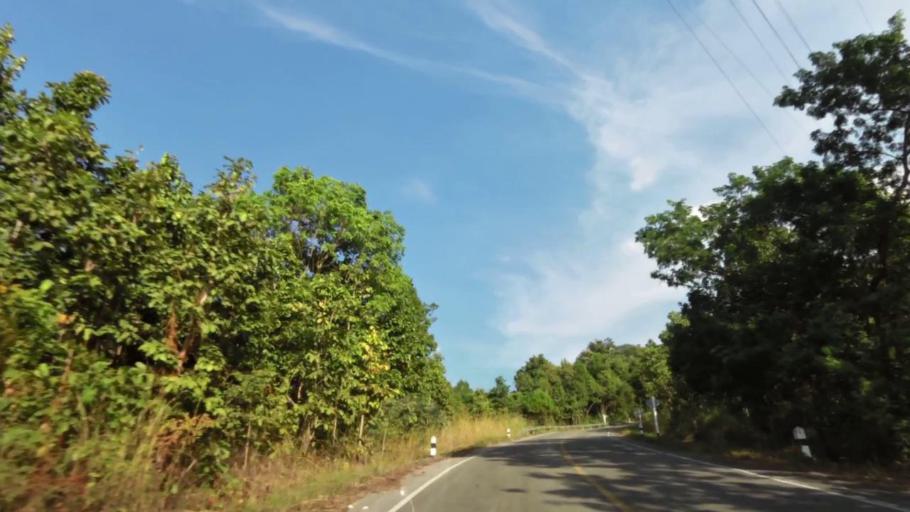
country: TH
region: Chiang Rai
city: Khun Tan
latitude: 19.8778
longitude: 100.3131
